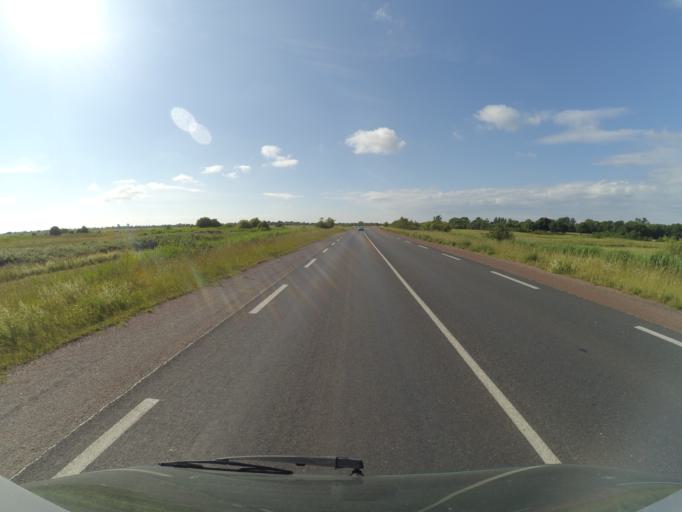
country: FR
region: Poitou-Charentes
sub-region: Departement de la Charente-Maritime
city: Saint-Agnant
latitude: 45.8575
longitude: -0.9653
